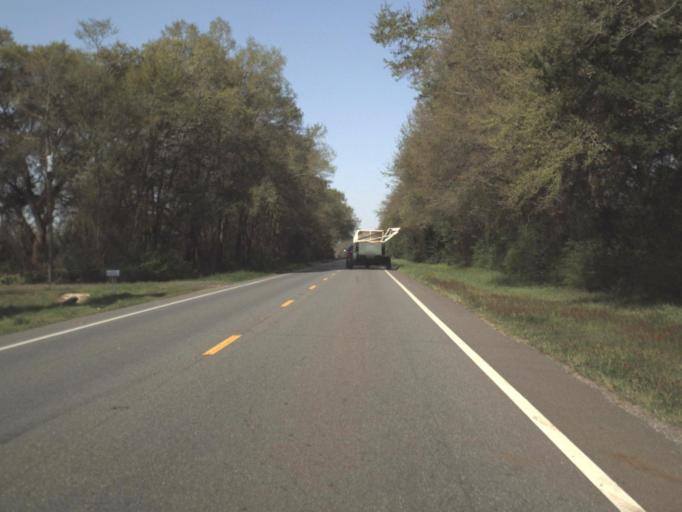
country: US
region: Alabama
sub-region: Houston County
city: Cottonwood
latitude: 30.9477
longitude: -85.3739
